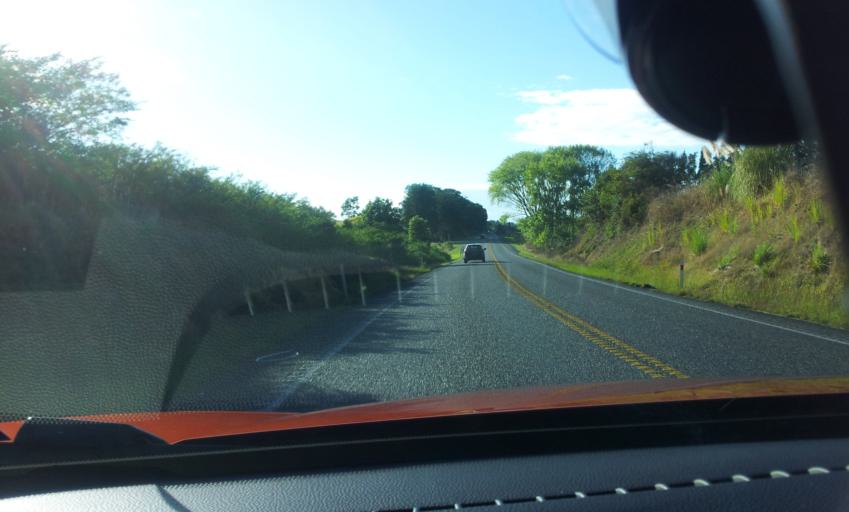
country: NZ
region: Waikato
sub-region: Hauraki District
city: Ngatea
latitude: -37.2807
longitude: 175.3601
